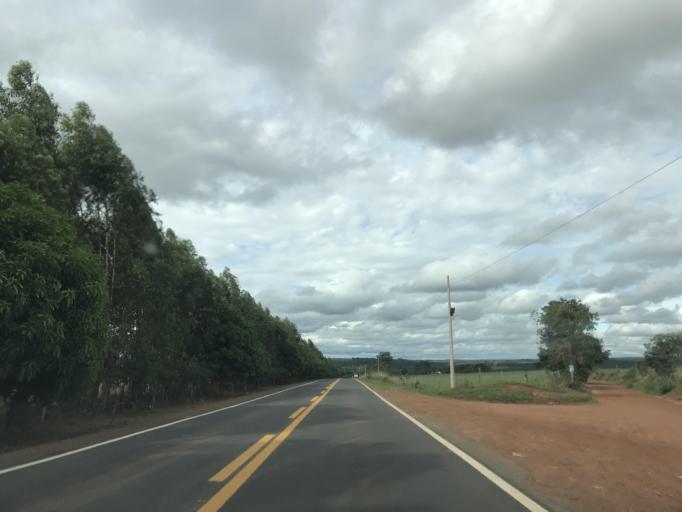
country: BR
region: Goias
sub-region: Bela Vista De Goias
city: Bela Vista de Goias
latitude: -17.1812
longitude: -48.6882
